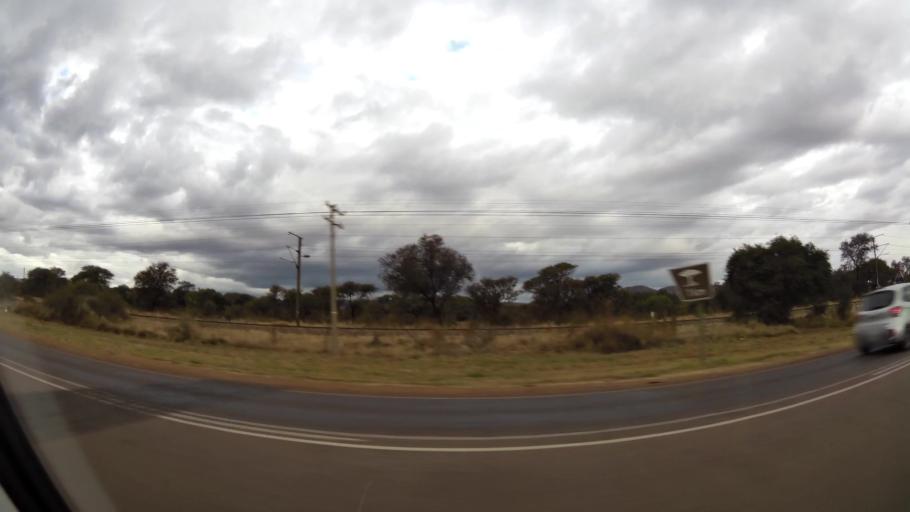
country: ZA
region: Limpopo
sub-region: Waterberg District Municipality
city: Mokopane
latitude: -24.2693
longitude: 28.9818
